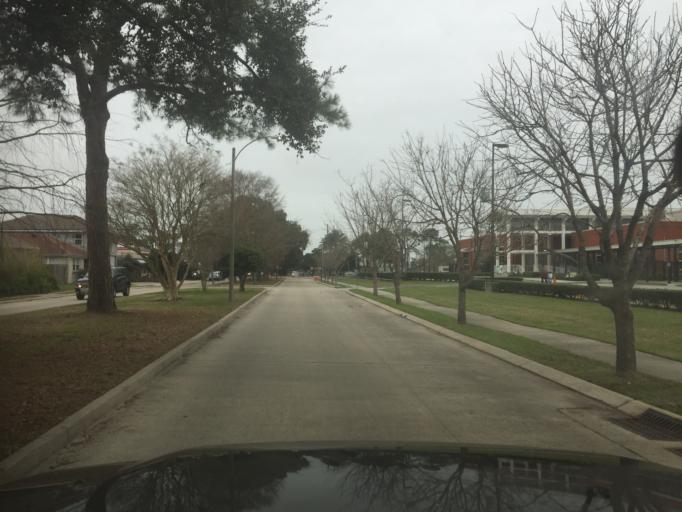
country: US
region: Louisiana
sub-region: Jefferson Parish
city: Metairie
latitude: 30.0028
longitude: -90.1028
